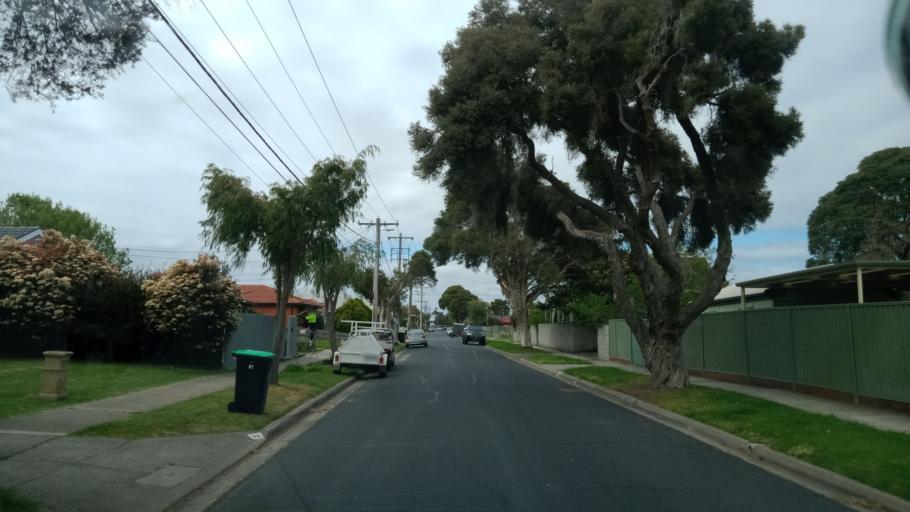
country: AU
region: Victoria
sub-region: Kingston
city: Edithvale
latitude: -38.0321
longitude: 145.1162
